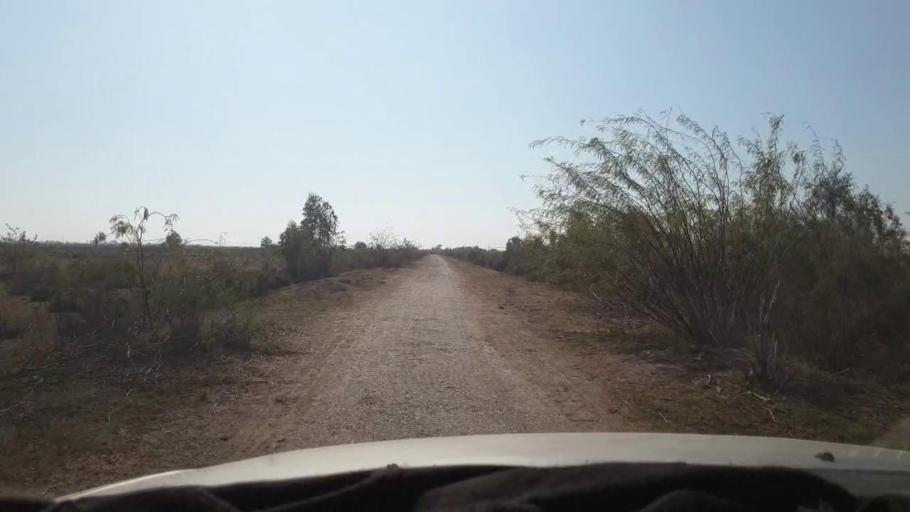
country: PK
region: Sindh
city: Adilpur
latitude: 27.8971
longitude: 69.2525
